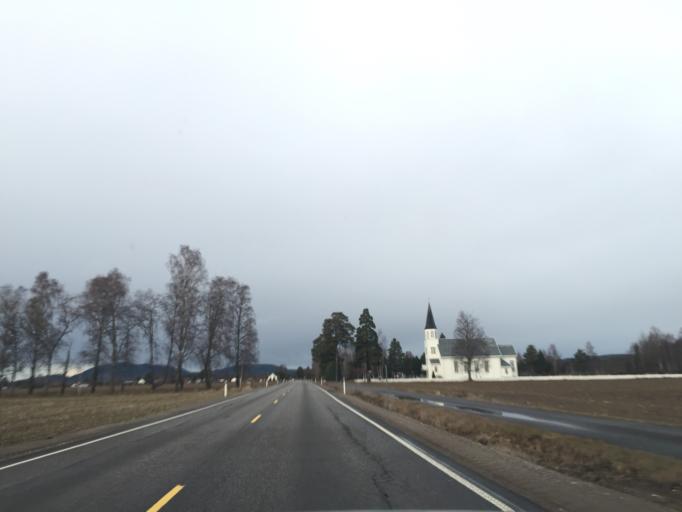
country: NO
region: Hedmark
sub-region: Asnes
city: Flisa
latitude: 60.5658
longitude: 12.0583
